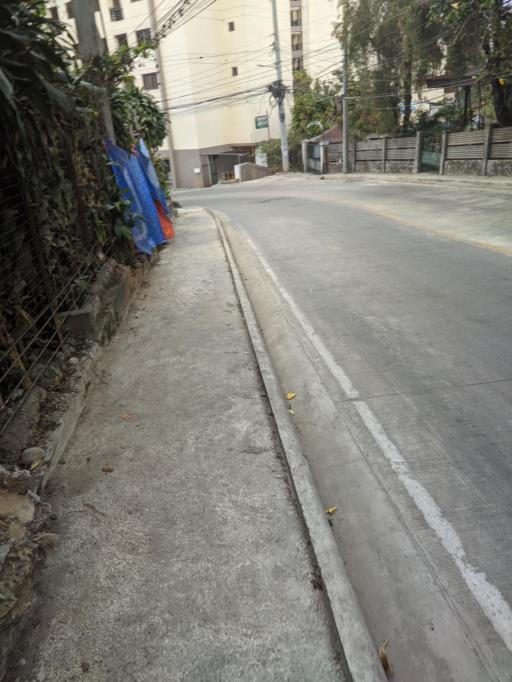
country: PH
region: Cordillera
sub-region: Baguio City
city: Baguio
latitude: 16.4128
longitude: 120.6013
